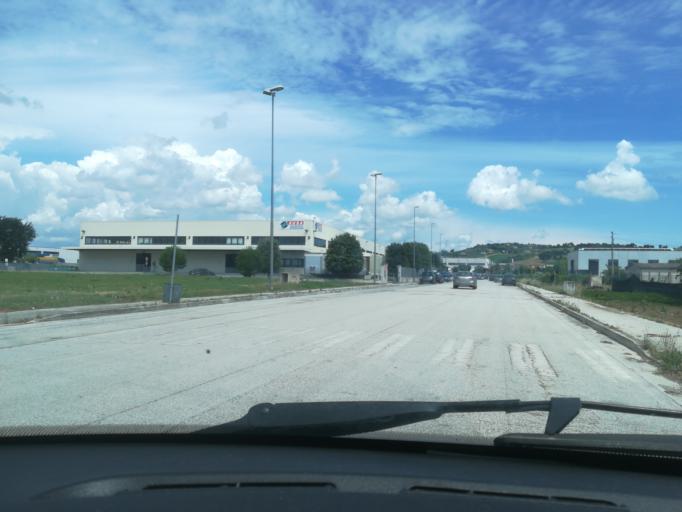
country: IT
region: The Marches
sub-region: Provincia di Macerata
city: Santa Maria Apparente
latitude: 43.2846
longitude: 13.6809
